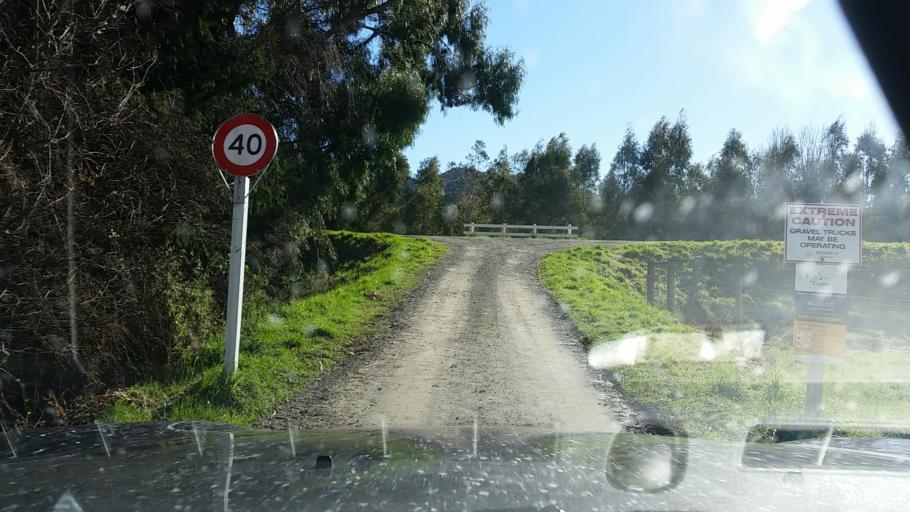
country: NZ
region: Marlborough
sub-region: Marlborough District
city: Blenheim
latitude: -41.4431
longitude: 173.9352
